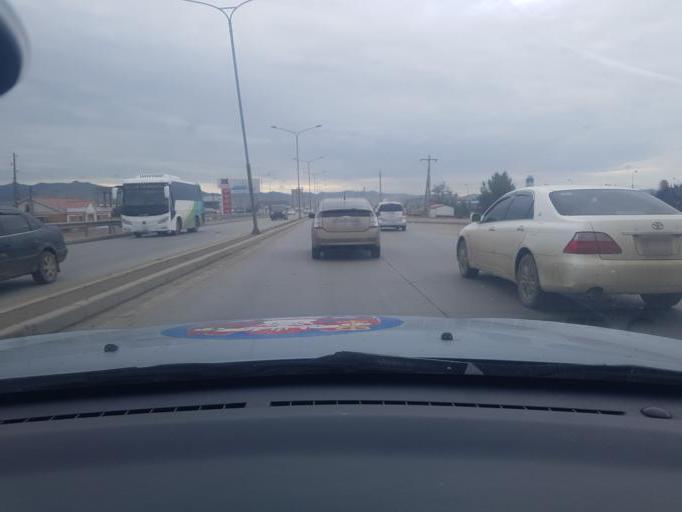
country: MN
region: Ulaanbaatar
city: Ulaanbaatar
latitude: 47.9006
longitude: 106.7857
